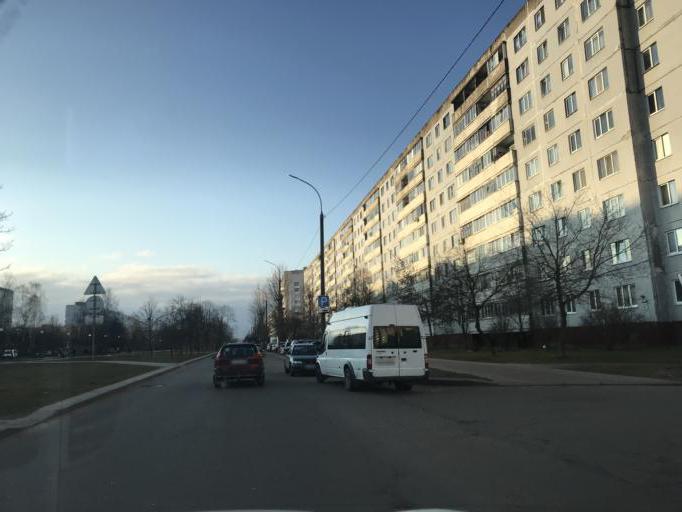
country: BY
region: Mogilev
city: Mahilyow
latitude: 53.8688
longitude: 30.3407
